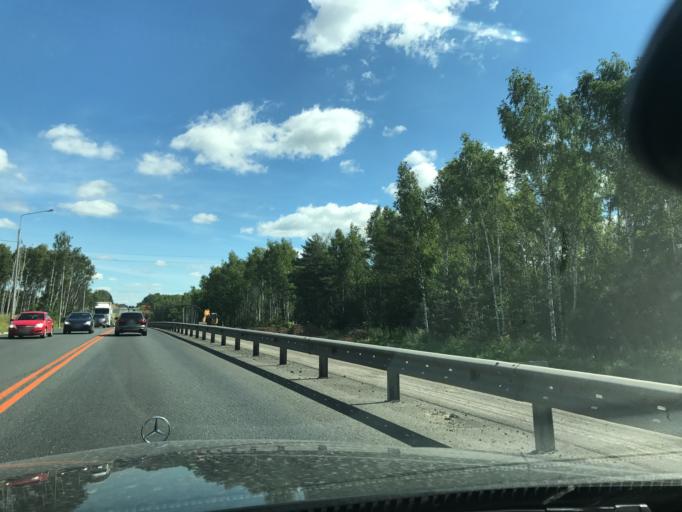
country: RU
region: Vladimir
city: Novovyazniki
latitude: 56.2031
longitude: 42.3202
